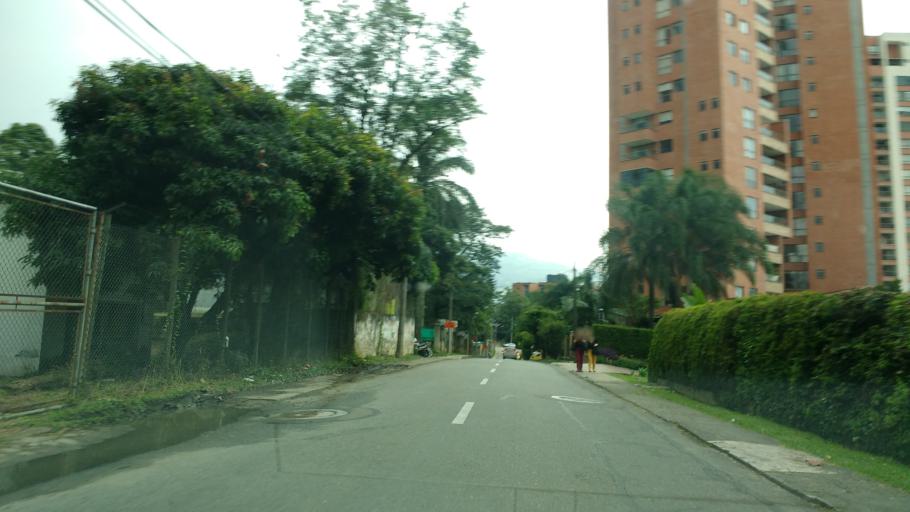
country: CO
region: Antioquia
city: Envigado
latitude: 6.1896
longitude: -75.5778
